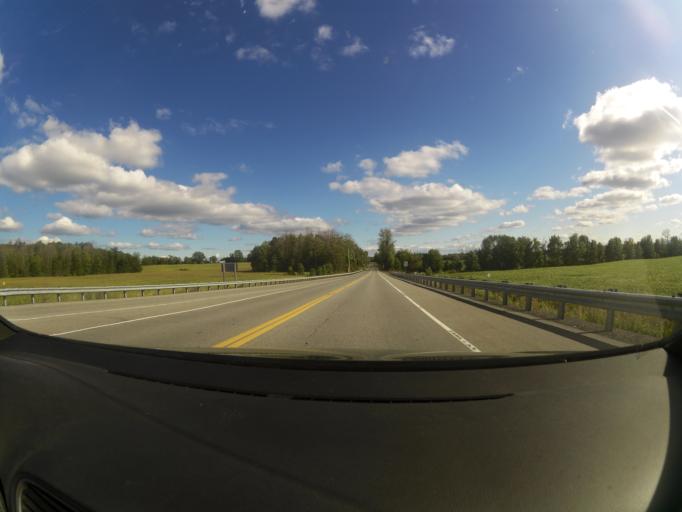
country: CA
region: Ontario
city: Carleton Place
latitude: 45.1484
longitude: -76.0889
